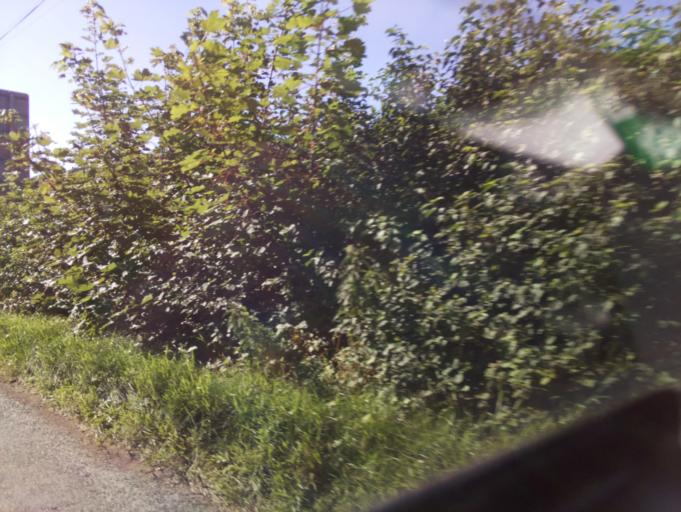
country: GB
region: England
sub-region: Herefordshire
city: Walford
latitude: 51.8657
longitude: -2.6063
